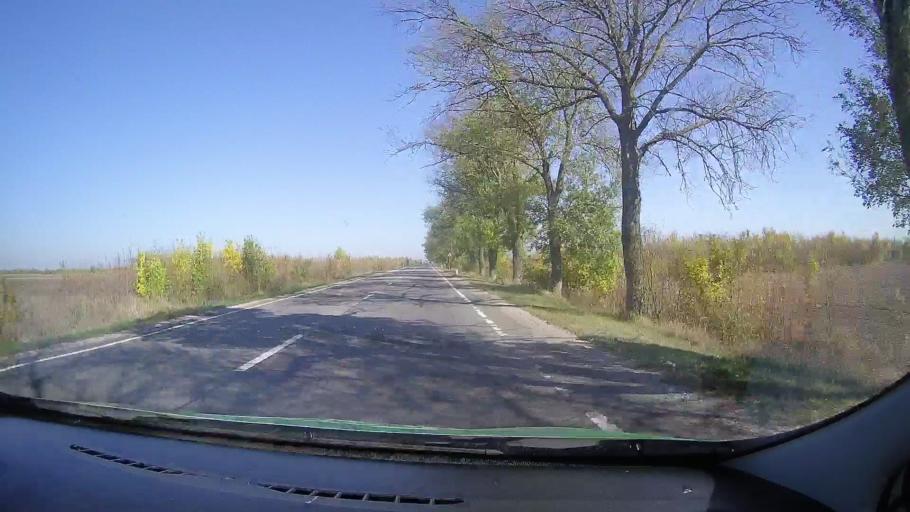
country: RO
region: Satu Mare
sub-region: Comuna Moftinu
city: Moftinu Mic
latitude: 47.7007
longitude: 22.6278
